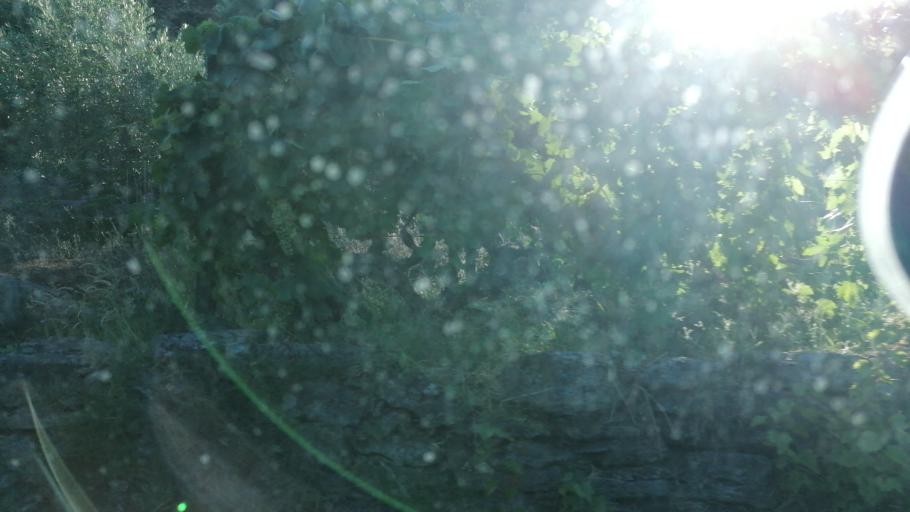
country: PT
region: Viseu
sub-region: Sao Joao da Pesqueira
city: Sao Joao da Pesqueira
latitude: 41.2395
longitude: -7.4312
